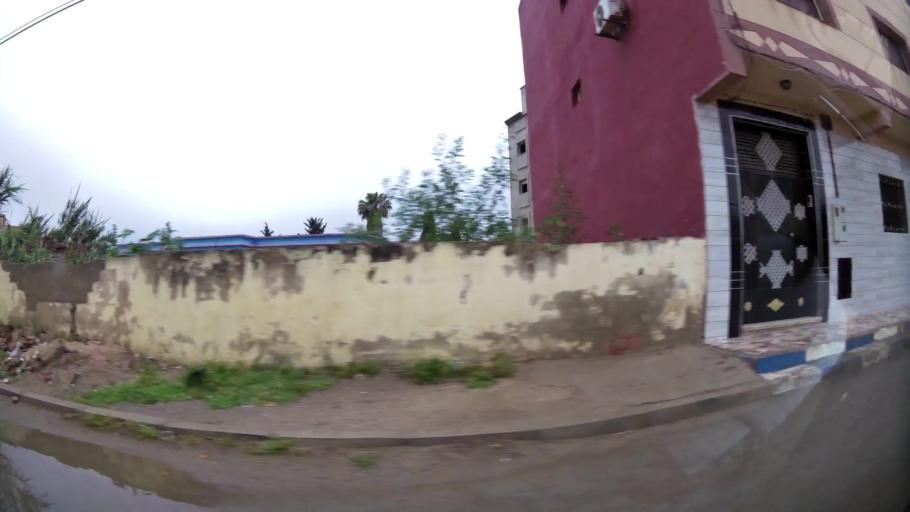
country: MA
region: Oriental
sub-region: Nador
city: Nador
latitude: 35.1620
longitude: -2.9535
